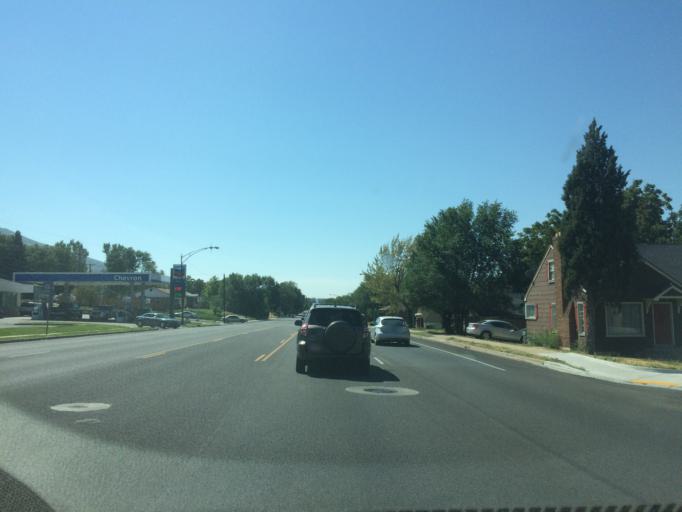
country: US
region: Utah
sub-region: Weber County
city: Ogden
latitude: 41.2298
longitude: -111.9481
